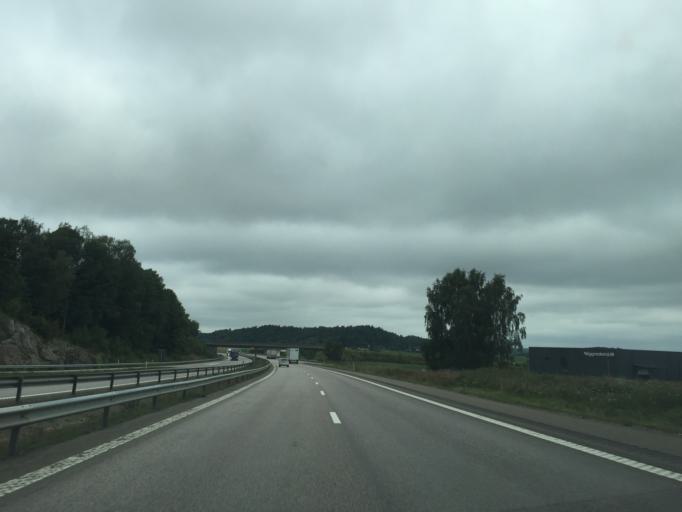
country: SE
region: Halland
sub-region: Kungsbacka Kommun
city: Fjaeras kyrkby
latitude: 57.4315
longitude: 12.1552
